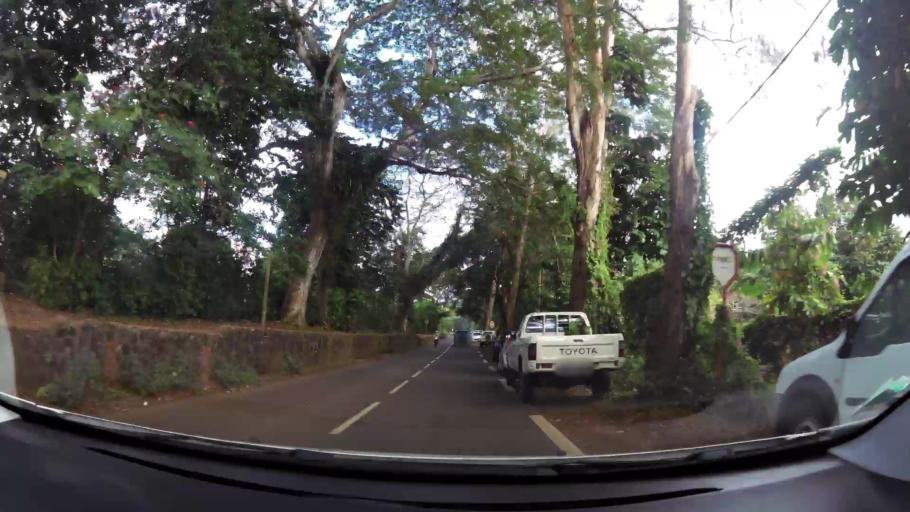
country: YT
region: Ouangani
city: Ouangani
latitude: -12.8340
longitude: 45.1368
